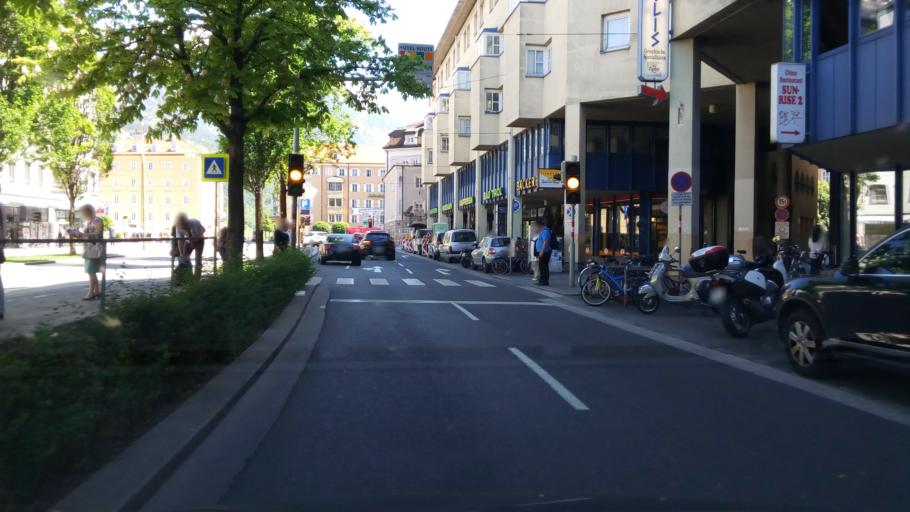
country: AT
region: Tyrol
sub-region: Innsbruck Stadt
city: Innsbruck
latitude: 47.2664
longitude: 11.3901
